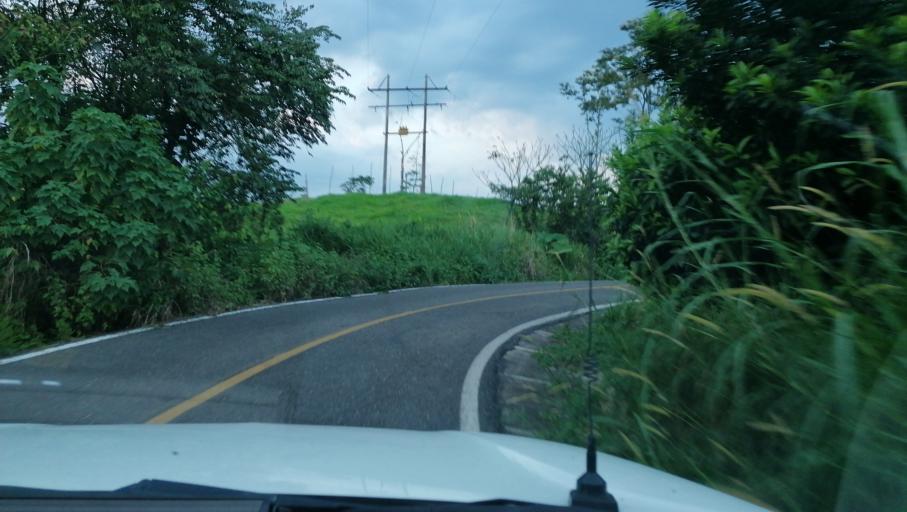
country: MX
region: Chiapas
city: Pichucalco
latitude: 17.5297
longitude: -93.1541
